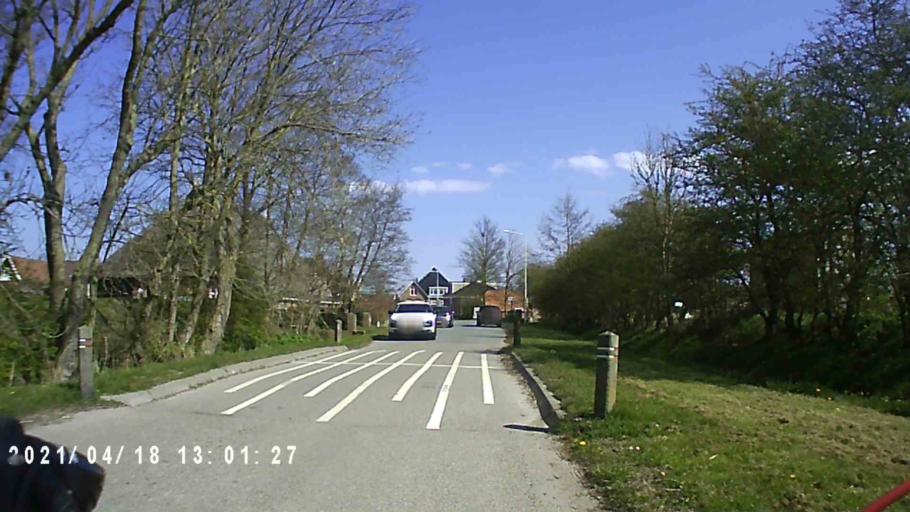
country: NL
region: Friesland
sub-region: Gemeente Dongeradeel
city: Anjum
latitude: 53.4007
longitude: 6.0863
